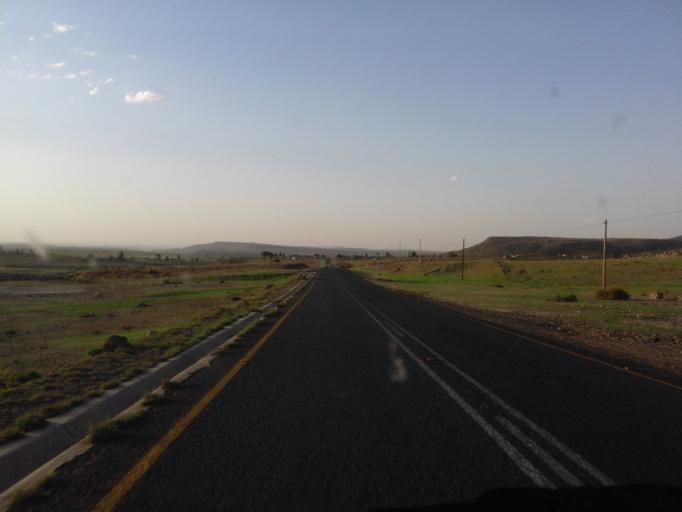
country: LS
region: Mafeteng
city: Mafeteng
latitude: -29.8914
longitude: 27.2544
